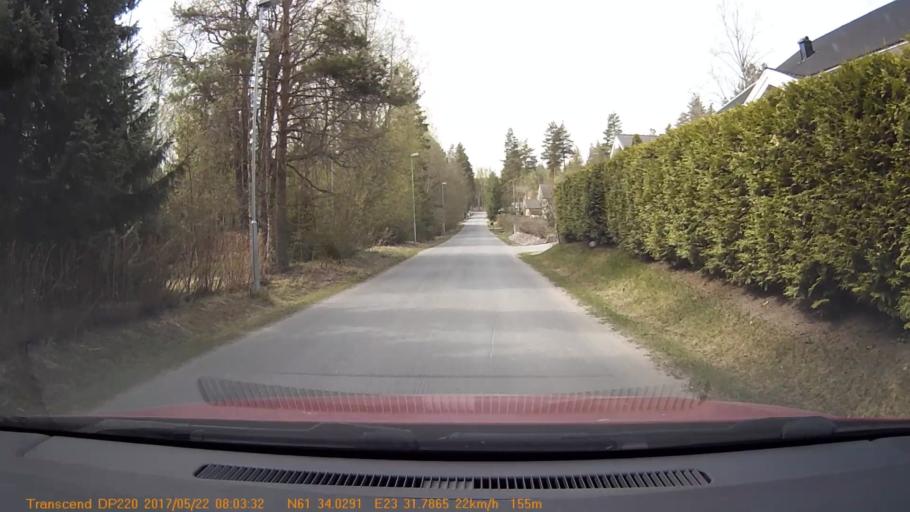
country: FI
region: Pirkanmaa
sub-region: Tampere
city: Yloejaervi
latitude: 61.5672
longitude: 23.5299
